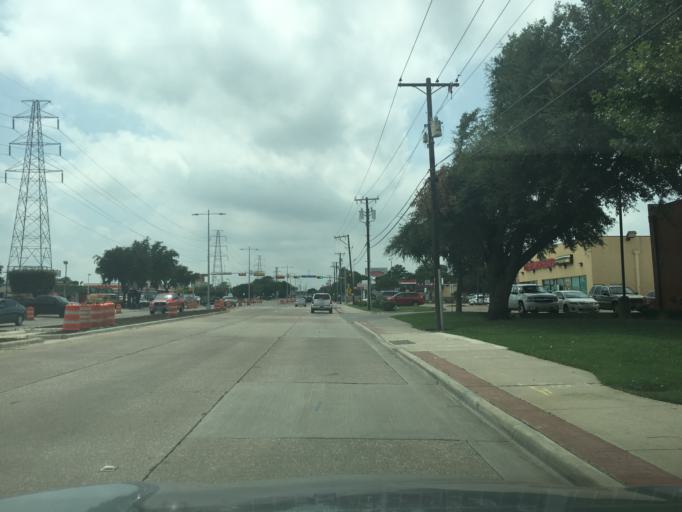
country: US
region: Texas
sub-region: Dallas County
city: Richardson
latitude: 32.9400
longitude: -96.7628
